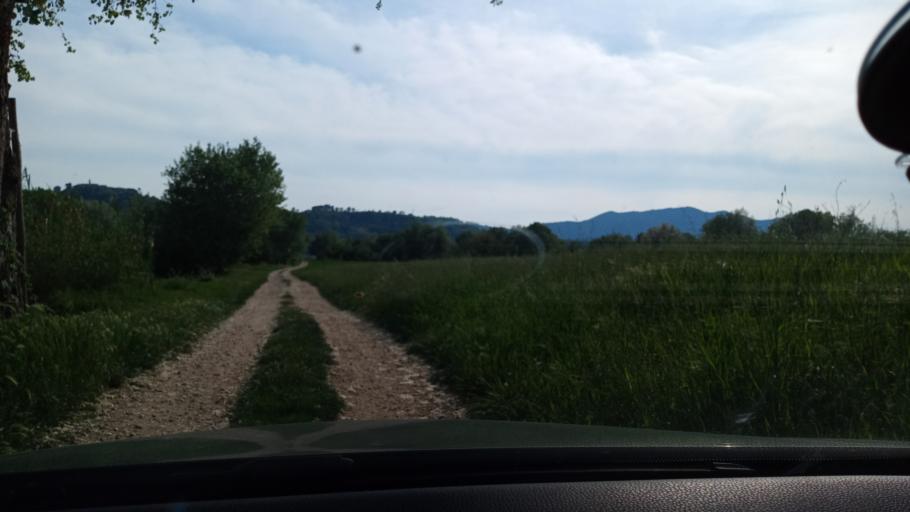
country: IT
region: Latium
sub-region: Citta metropolitana di Roma Capitale
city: Ponzano Romano
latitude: 42.2766
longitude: 12.5794
